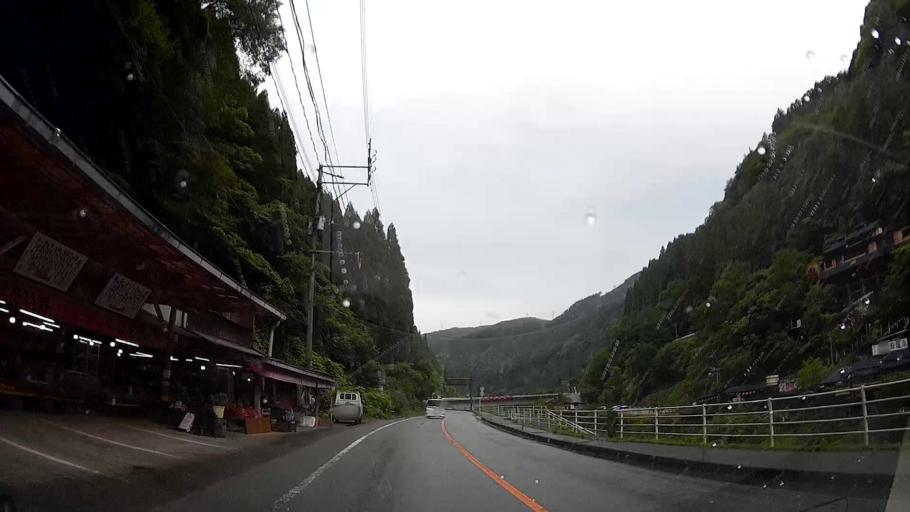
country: JP
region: Oita
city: Tsukawaki
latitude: 33.1733
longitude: 131.0370
